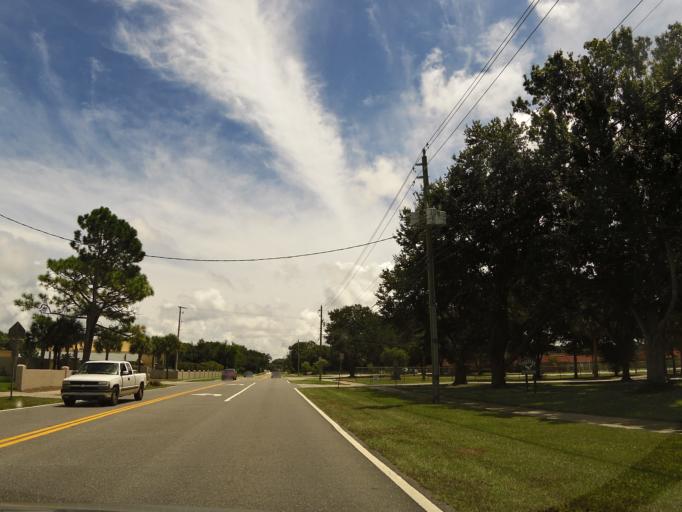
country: US
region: Florida
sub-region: Brevard County
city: Mims
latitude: 28.6371
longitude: -80.8510
